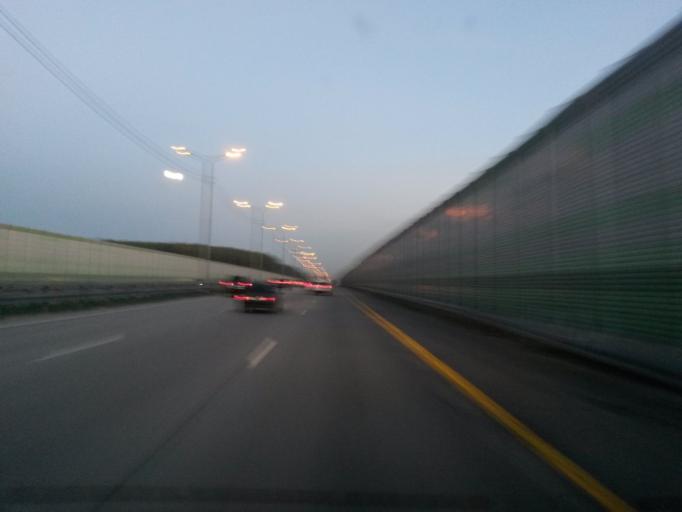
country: RU
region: Moskovskaya
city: Belyye Stolby
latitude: 55.3076
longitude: 37.8273
